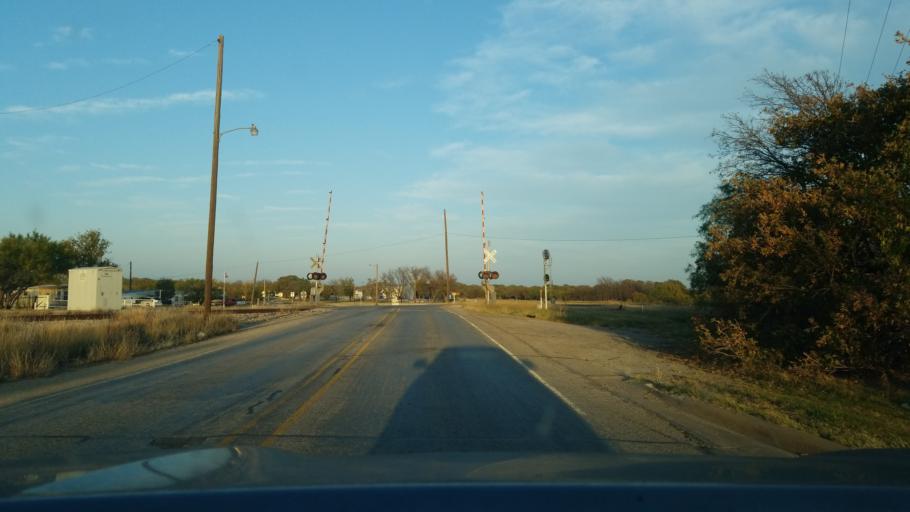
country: US
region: Texas
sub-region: Eastland County
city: Cisco
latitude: 32.3918
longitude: -98.9757
